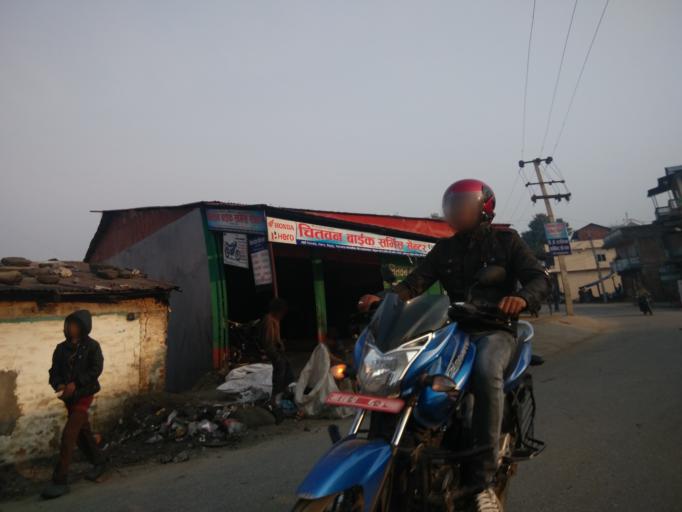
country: NP
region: Central Region
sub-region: Narayani Zone
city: Bharatpur
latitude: 27.6907
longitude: 84.4266
